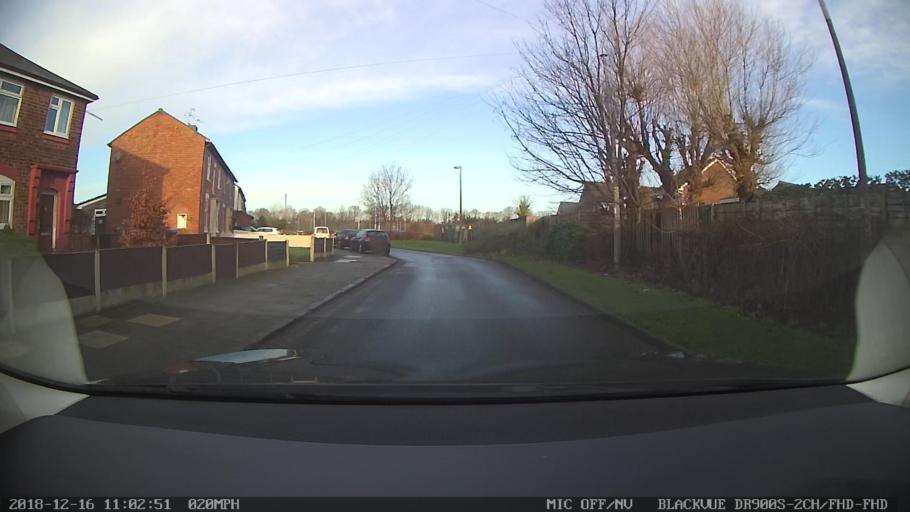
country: GB
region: England
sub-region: Manchester
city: Swinton
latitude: 53.4811
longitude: -2.3706
